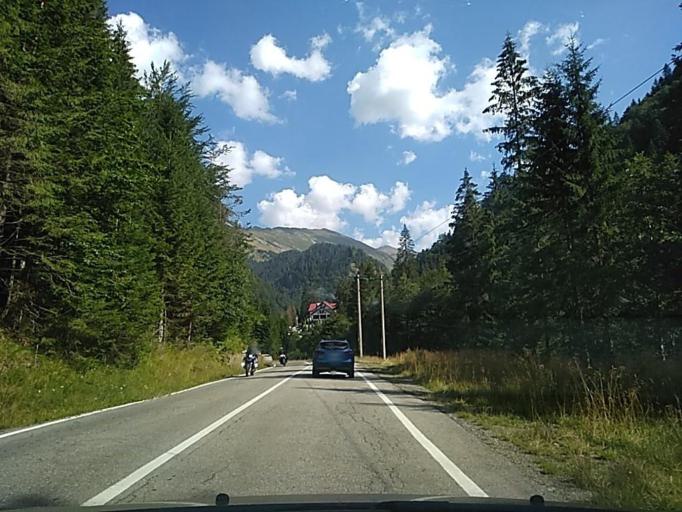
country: RO
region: Sibiu
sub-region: Comuna Cartisoara
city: Cartisoara
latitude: 45.5517
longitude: 24.6002
